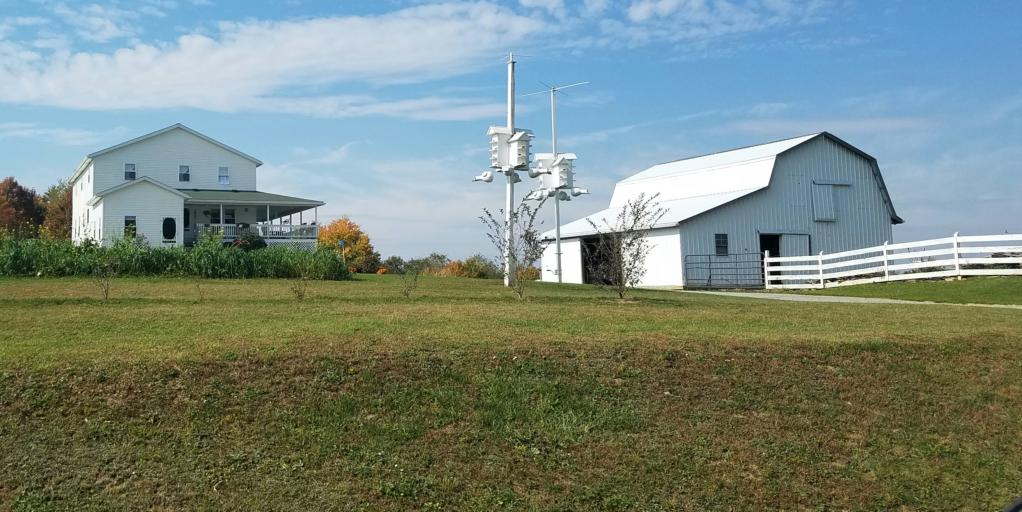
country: US
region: Pennsylvania
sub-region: Clarion County
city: Knox
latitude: 41.2380
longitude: -79.5683
